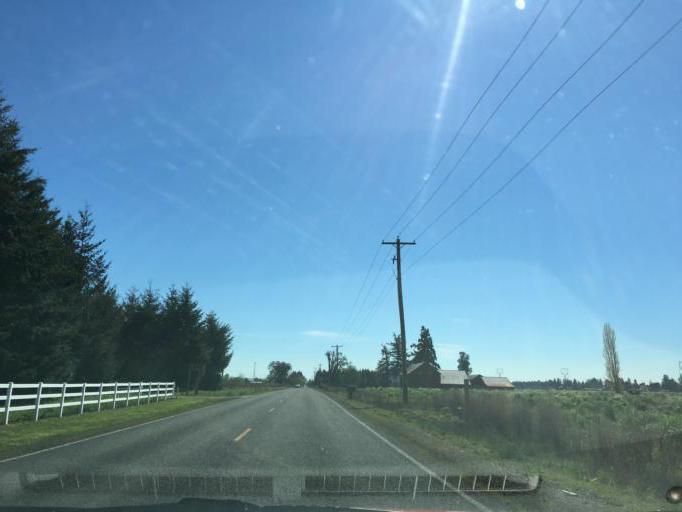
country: US
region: Oregon
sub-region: Clackamas County
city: Canby
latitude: 45.1842
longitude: -122.7226
